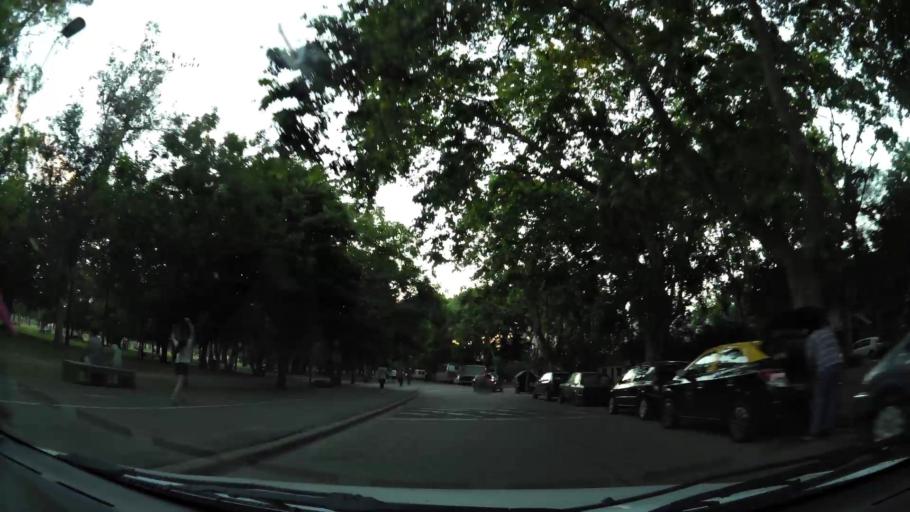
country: AR
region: Buenos Aires F.D.
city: Colegiales
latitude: -34.5494
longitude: -58.4812
